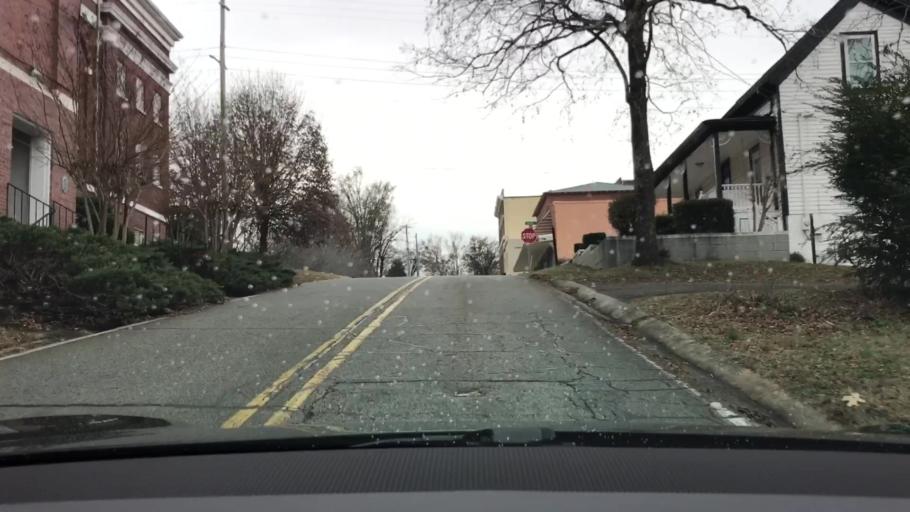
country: US
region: Georgia
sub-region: Gwinnett County
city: Buford
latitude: 34.1189
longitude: -84.0051
